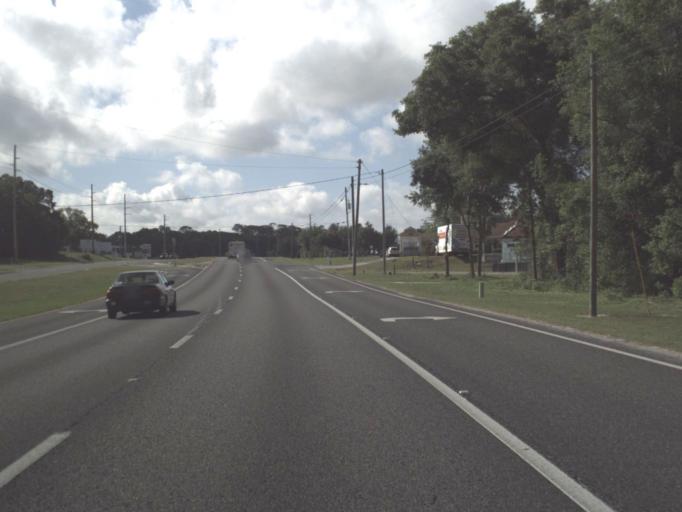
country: US
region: Florida
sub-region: Lake County
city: Lady Lake
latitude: 28.9024
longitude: -81.9141
